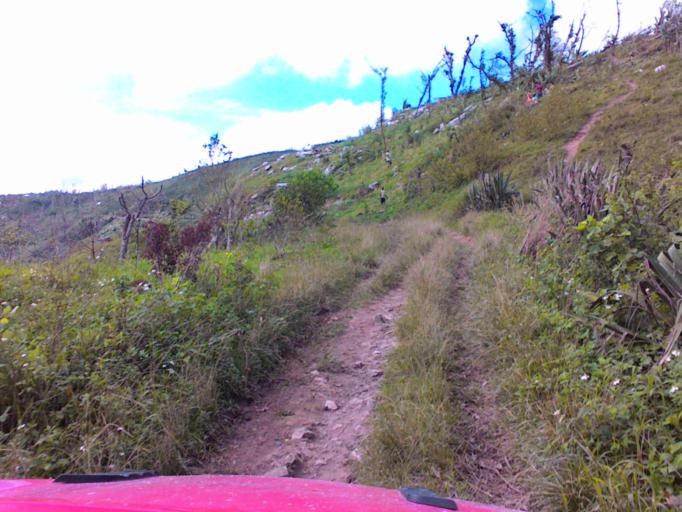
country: HT
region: Grandans
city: Moron
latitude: 18.4619
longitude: -74.1141
